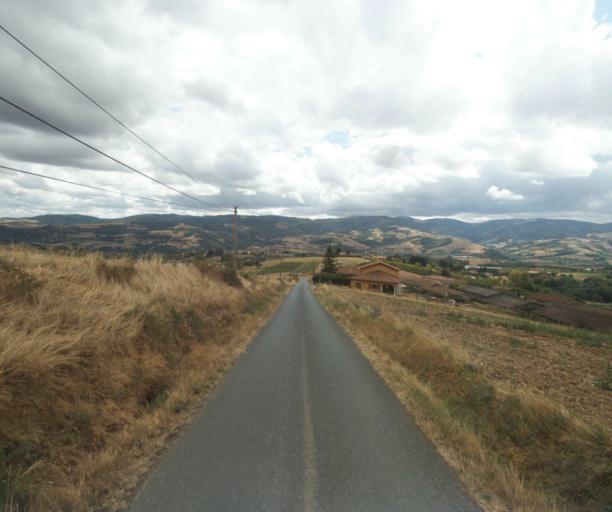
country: FR
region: Rhone-Alpes
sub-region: Departement du Rhone
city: Bessenay
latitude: 45.7819
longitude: 4.5363
